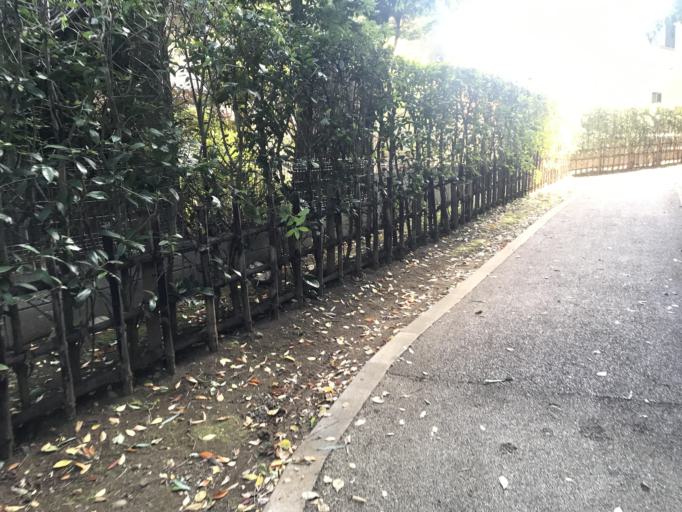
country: JP
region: Tokyo
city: Higashimurayama-shi
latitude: 35.7471
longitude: 139.4889
